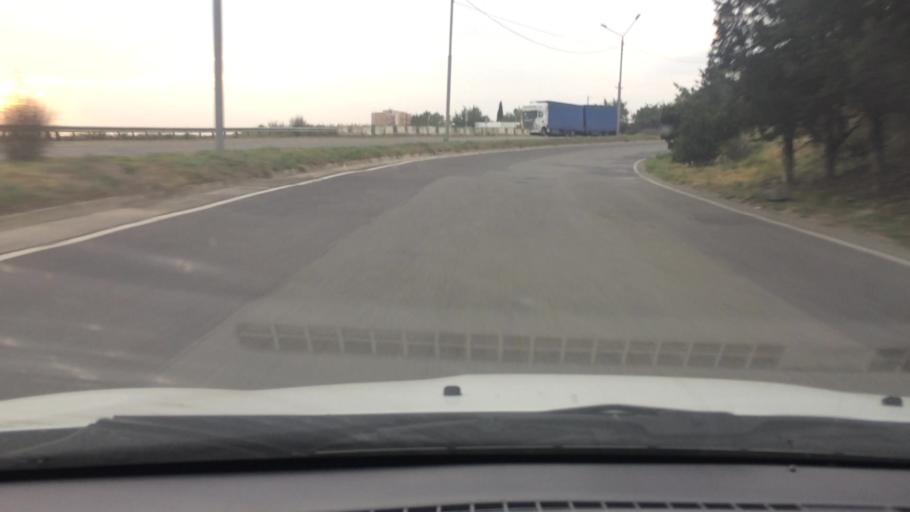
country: GE
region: T'bilisi
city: Tbilisi
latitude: 41.6516
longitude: 44.9041
